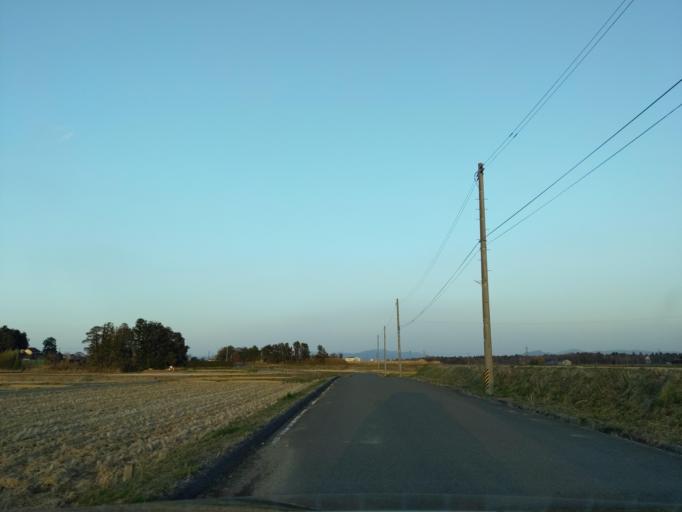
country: JP
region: Fukushima
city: Koriyama
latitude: 37.3419
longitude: 140.3183
